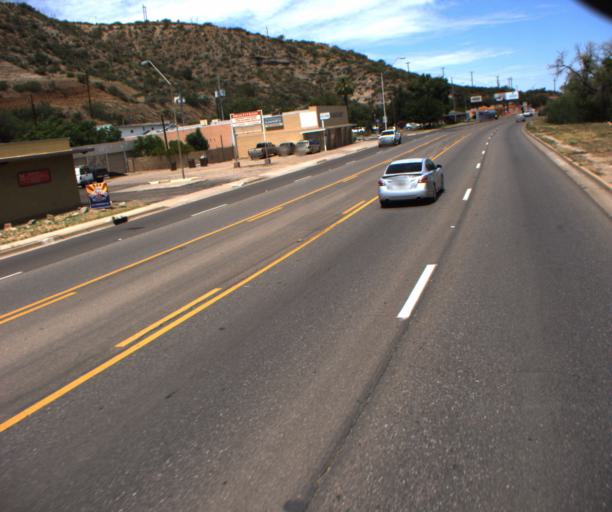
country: US
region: Arizona
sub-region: Gila County
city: Globe
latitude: 33.4088
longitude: -110.7938
